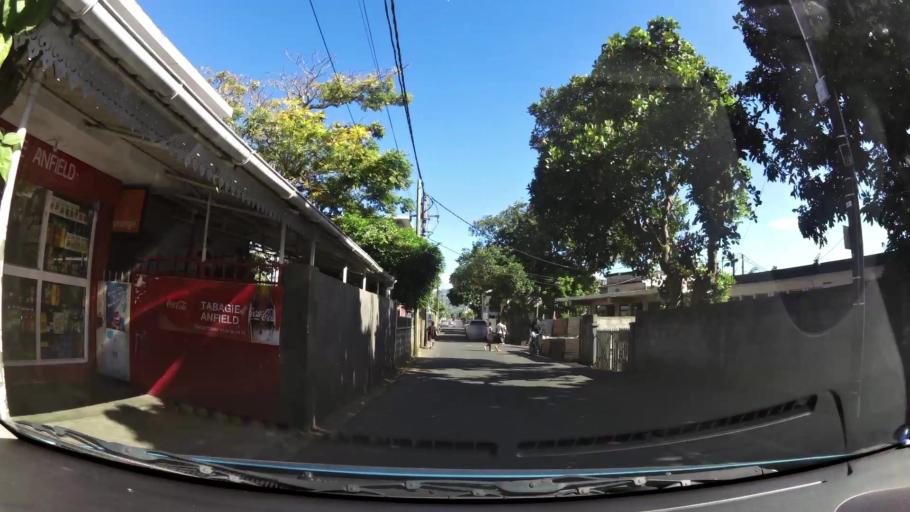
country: MU
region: Plaines Wilhems
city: Quatre Bornes
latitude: -20.2770
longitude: 57.4702
